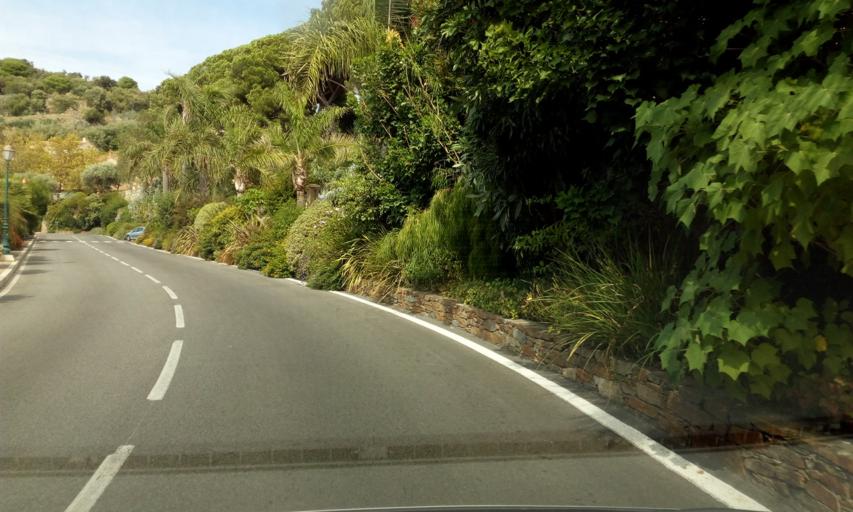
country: FR
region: Provence-Alpes-Cote d'Azur
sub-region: Departement du Var
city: Bormes-les-Mimosas
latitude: 43.1506
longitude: 6.3439
